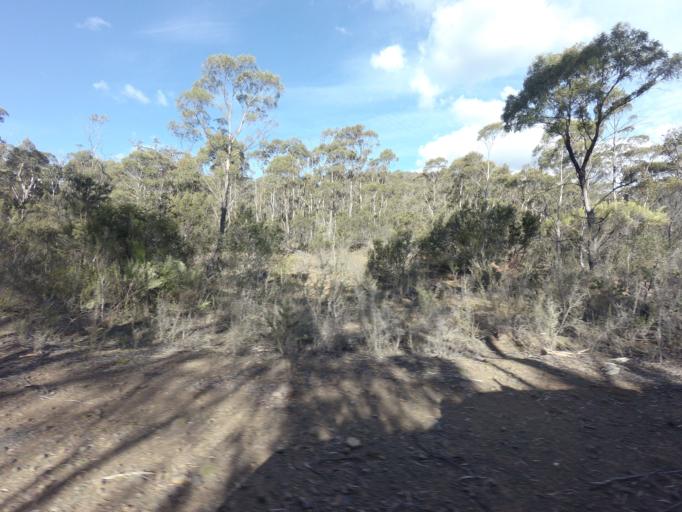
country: AU
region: Tasmania
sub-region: Break O'Day
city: St Helens
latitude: -41.8589
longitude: 148.0239
